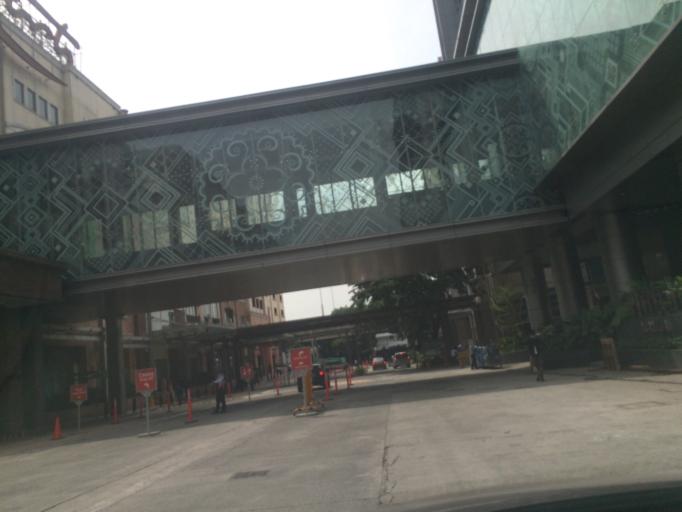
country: PH
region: Metro Manila
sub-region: Makati City
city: Makati City
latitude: 14.5190
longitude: 121.0191
